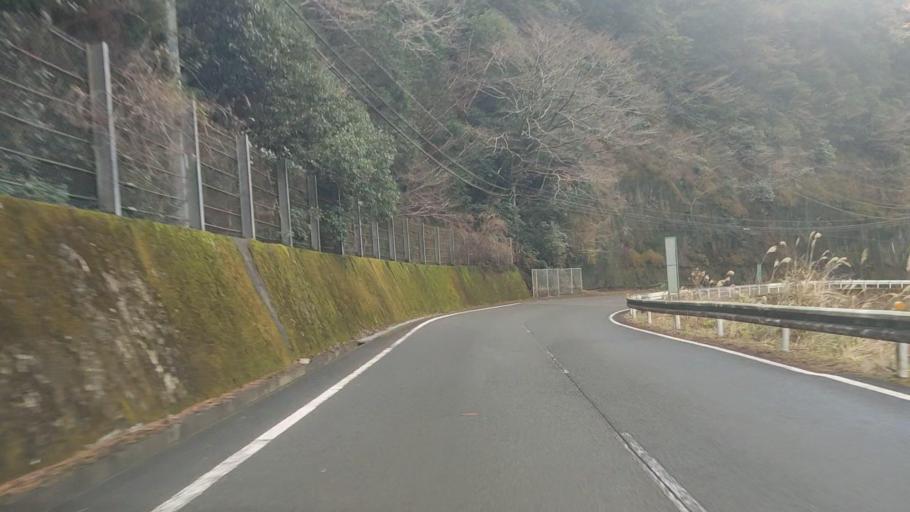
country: JP
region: Kumamoto
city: Hitoyoshi
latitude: 32.4249
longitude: 130.8568
